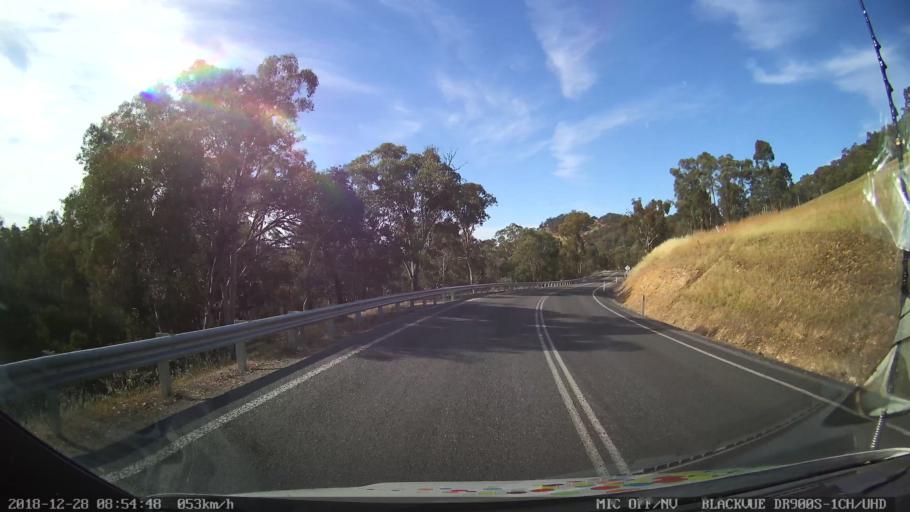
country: AU
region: New South Wales
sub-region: Upper Lachlan Shire
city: Crookwell
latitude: -34.0951
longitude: 149.3327
